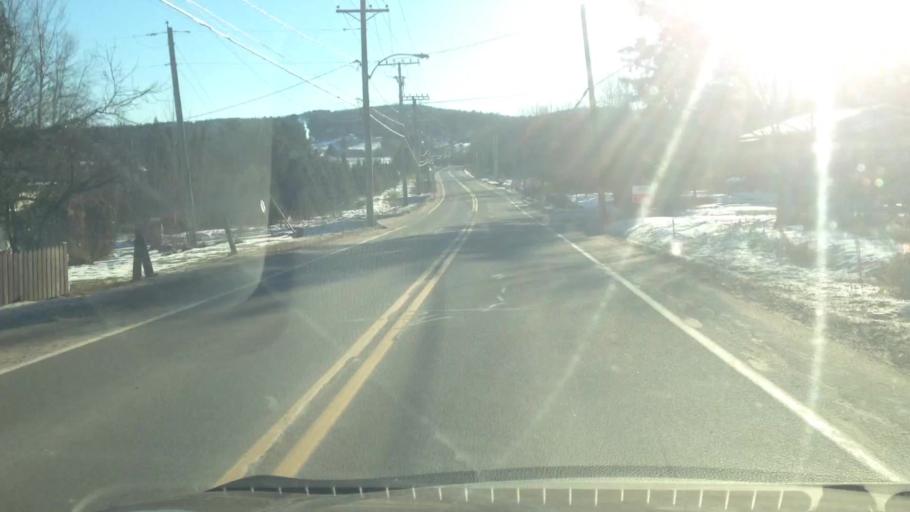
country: CA
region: Quebec
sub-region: Laurentides
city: Mont-Tremblant
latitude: 45.9749
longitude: -74.6146
